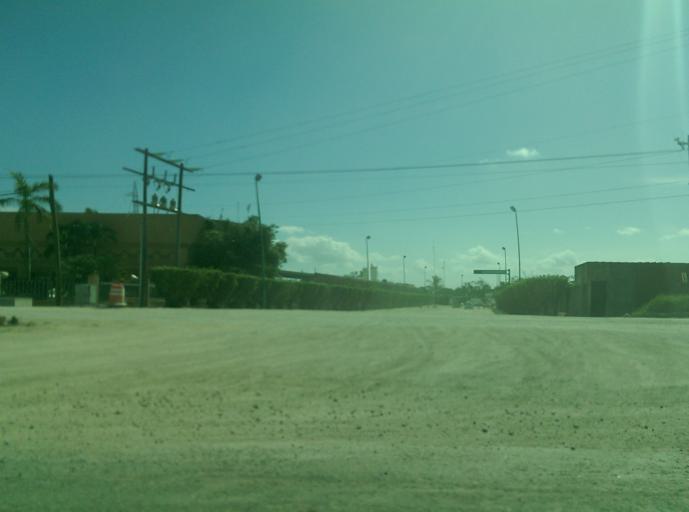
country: MX
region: Tabasco
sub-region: Centro
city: Anacleto Canabal 3ra. Seccion
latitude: 17.9867
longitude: -92.9907
